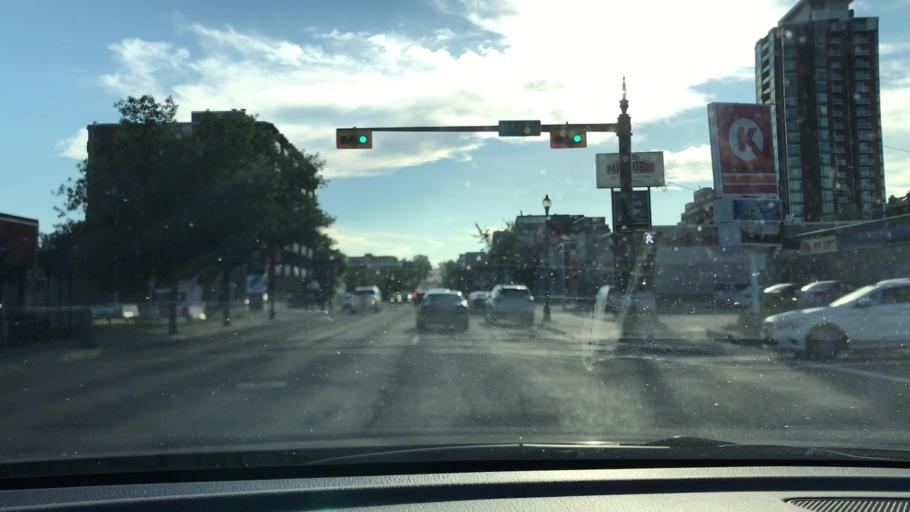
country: CA
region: Alberta
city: Calgary
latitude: 51.0379
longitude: -114.0891
